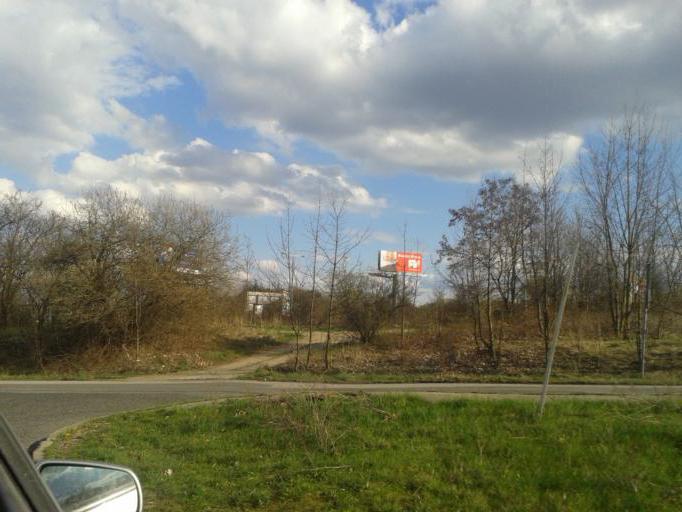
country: CZ
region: Central Bohemia
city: Hostivice
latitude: 50.0533
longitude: 14.3036
